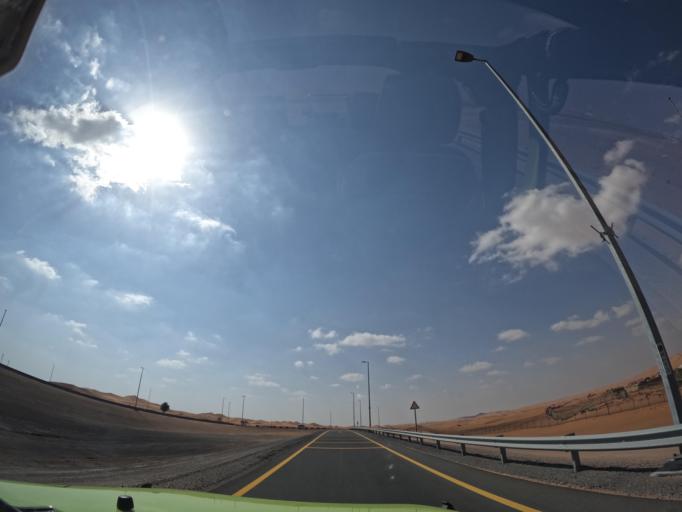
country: AE
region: Ash Shariqah
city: Adh Dhayd
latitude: 24.9423
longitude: 55.7315
